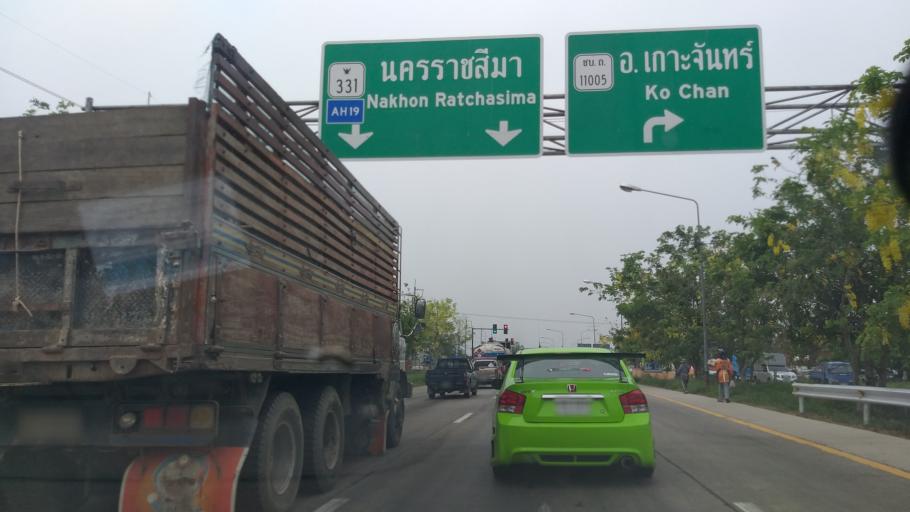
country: TH
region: Chon Buri
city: Ko Chan
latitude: 13.3868
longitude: 101.2789
